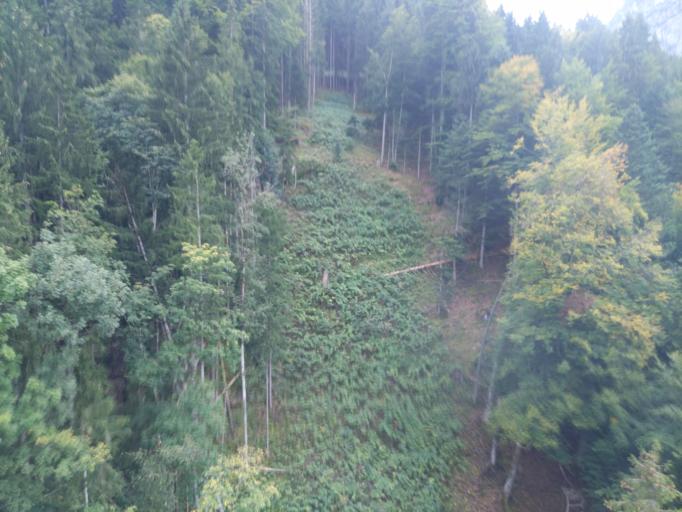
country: DE
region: Bavaria
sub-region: Upper Bavaria
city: Grainau
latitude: 47.4679
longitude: 11.0604
